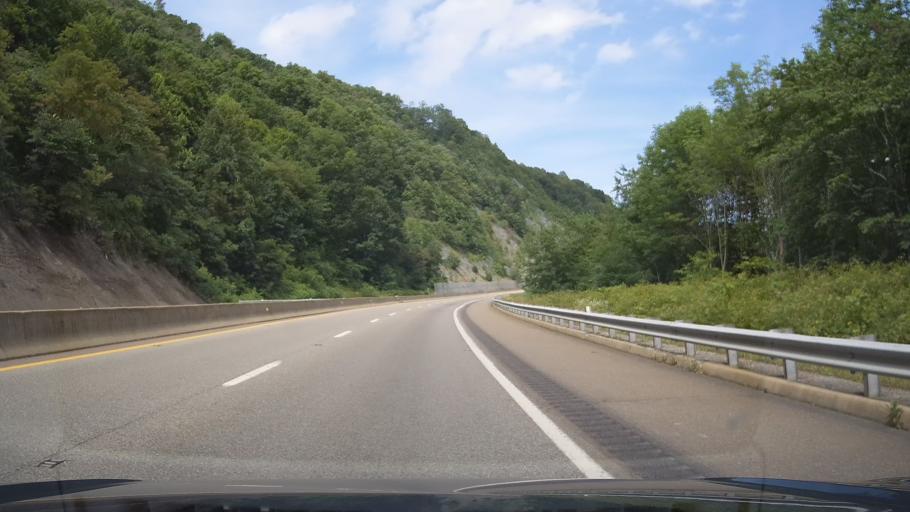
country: US
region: Virginia
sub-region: City of Norton
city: Norton
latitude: 36.9094
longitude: -82.6821
